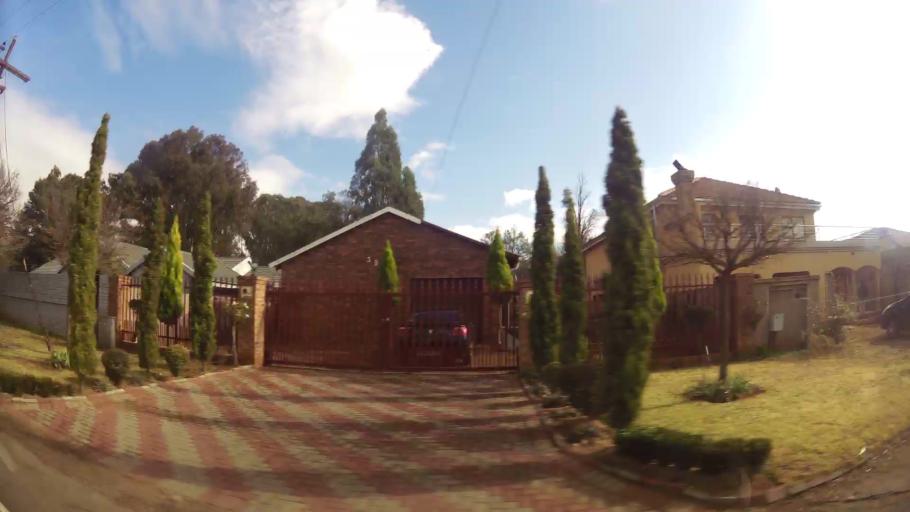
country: ZA
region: Gauteng
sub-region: Sedibeng District Municipality
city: Meyerton
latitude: -26.5514
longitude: 28.0568
